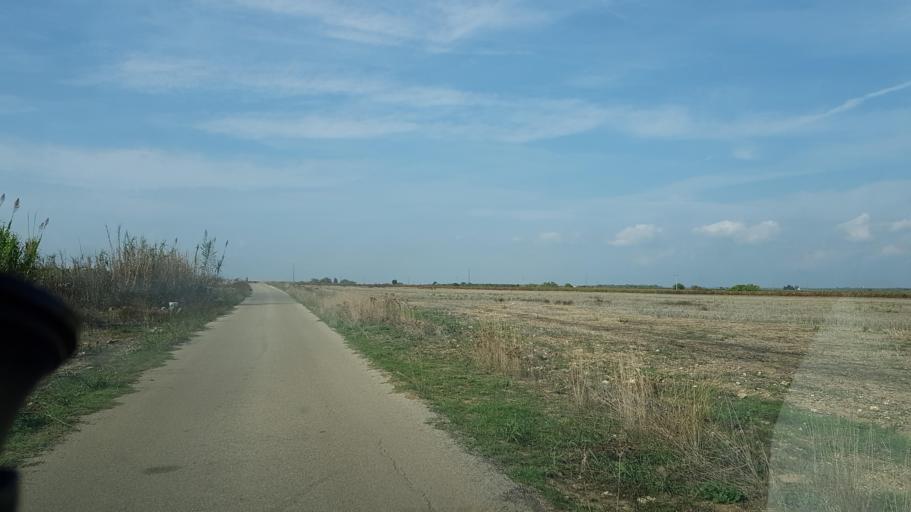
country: IT
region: Apulia
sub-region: Provincia di Brindisi
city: San Pancrazio Salentino
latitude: 40.4303
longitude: 17.8551
